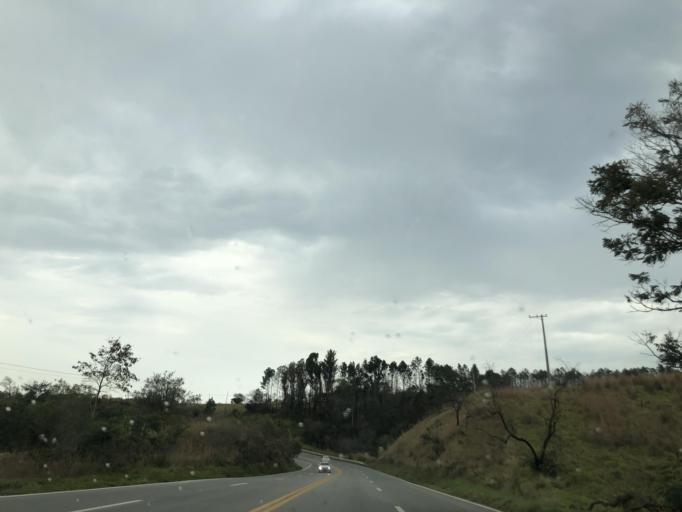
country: BR
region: Sao Paulo
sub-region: Salto De Pirapora
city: Salto de Pirapora
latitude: -23.6935
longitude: -47.6087
